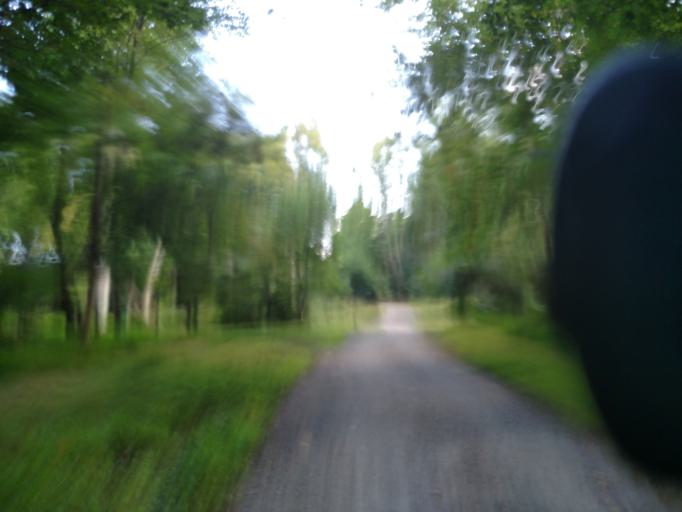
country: US
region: Virginia
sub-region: Fairfax County
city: Ravensworth
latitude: 38.8259
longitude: -77.2239
